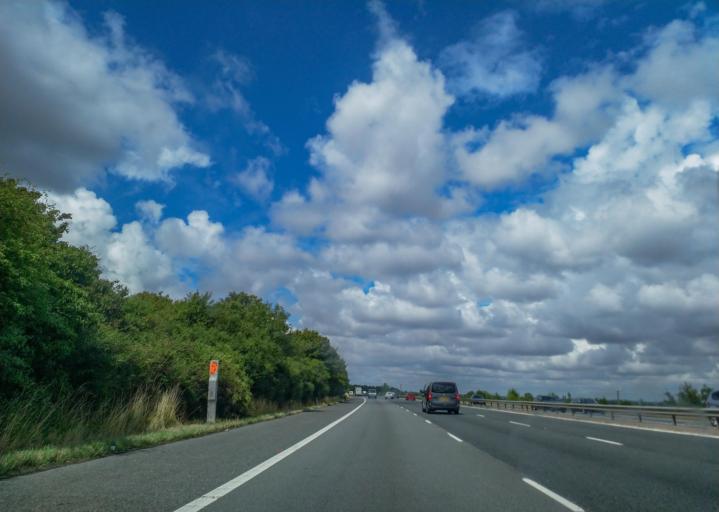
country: GB
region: England
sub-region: Oxfordshire
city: Bicester
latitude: 51.8380
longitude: -1.1352
